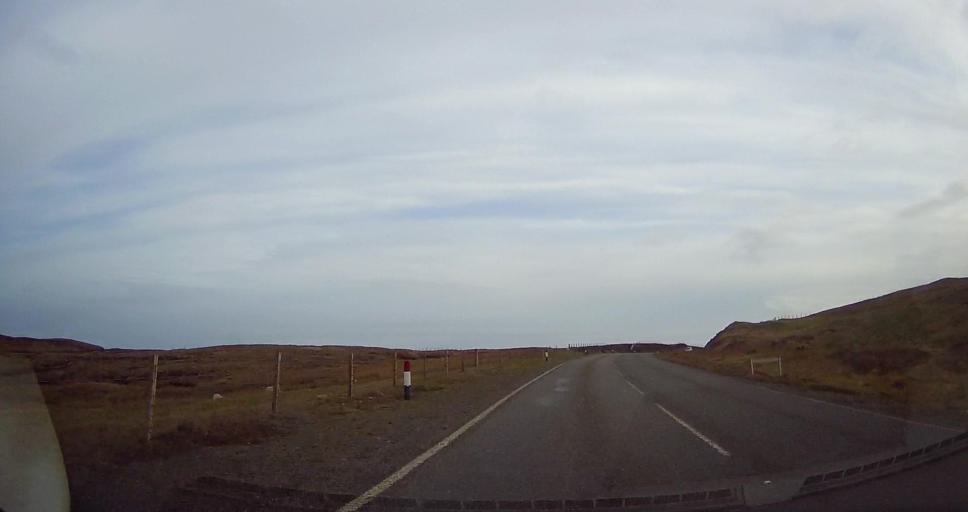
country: GB
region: Scotland
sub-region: Shetland Islands
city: Sandwick
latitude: 60.0912
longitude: -1.2282
